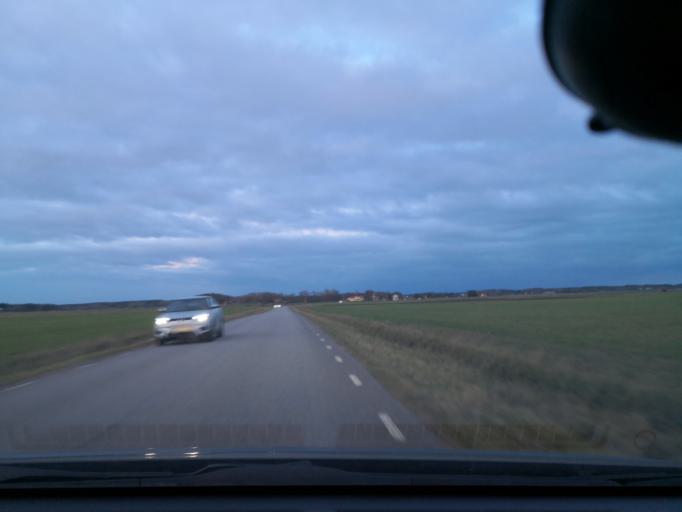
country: SE
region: Uppsala
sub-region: Enkopings Kommun
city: Irsta
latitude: 59.6880
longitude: 16.9617
